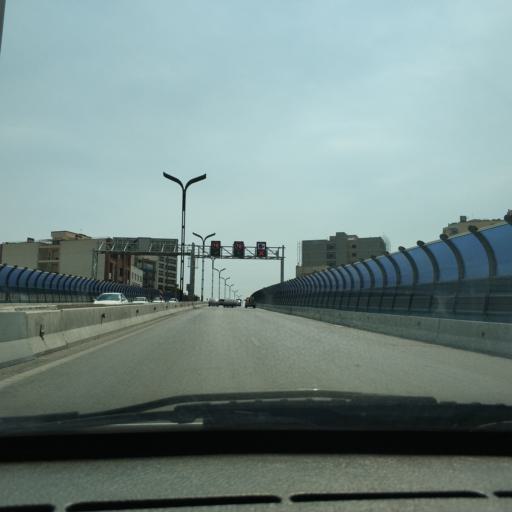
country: IR
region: Tehran
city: Tajrish
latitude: 35.7889
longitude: 51.4521
